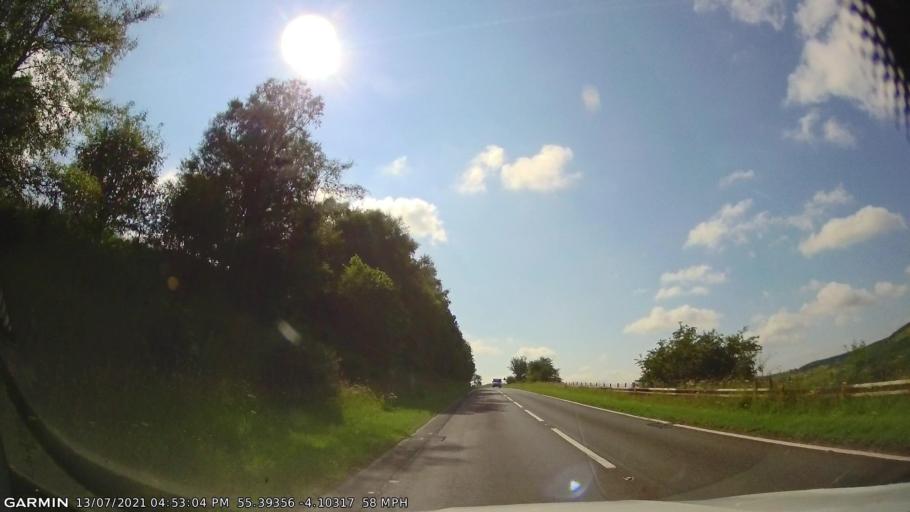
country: GB
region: Scotland
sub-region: East Ayrshire
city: New Cumnock
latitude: 55.3935
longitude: -4.1028
